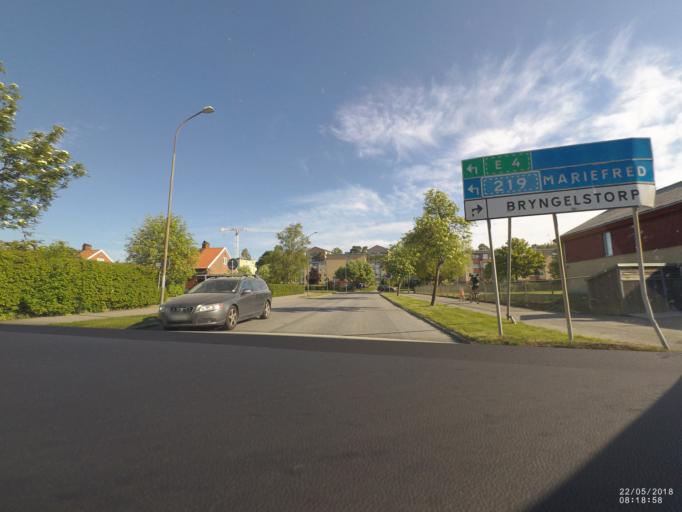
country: SE
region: Soedermanland
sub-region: Nykopings Kommun
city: Nykoping
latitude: 58.7535
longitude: 17.0435
